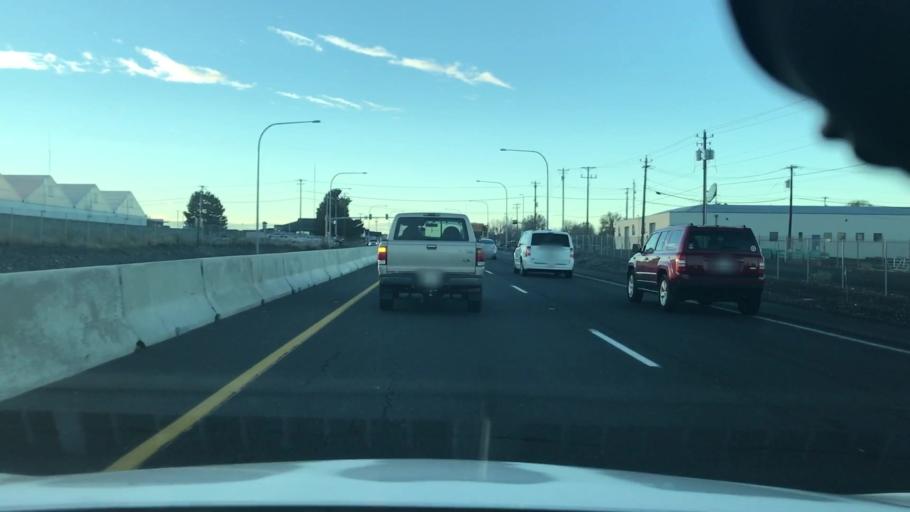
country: US
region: Washington
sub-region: Grant County
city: Moses Lake
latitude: 47.1330
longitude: -119.2569
